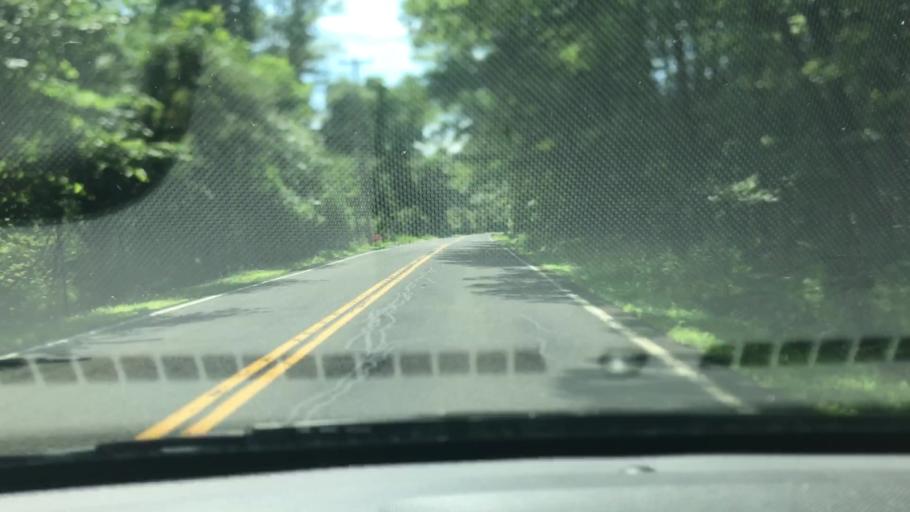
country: US
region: New York
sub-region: Ulster County
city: Shokan
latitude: 41.9165
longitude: -74.1836
